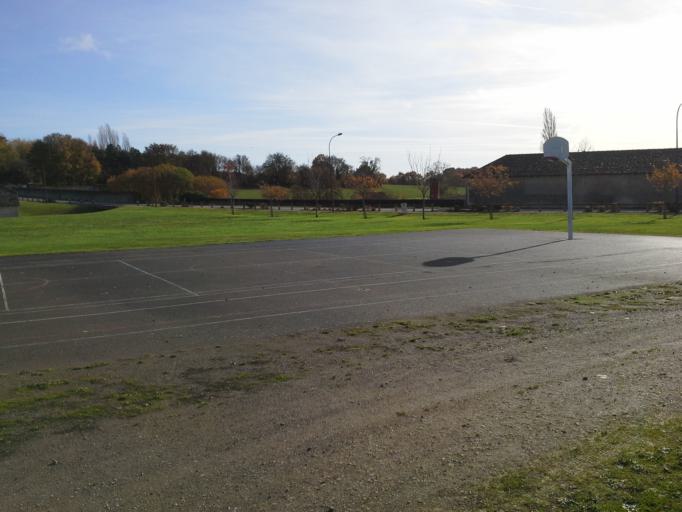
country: FR
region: Poitou-Charentes
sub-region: Departement de la Vienne
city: Pleumartin
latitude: 46.6433
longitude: 0.7543
